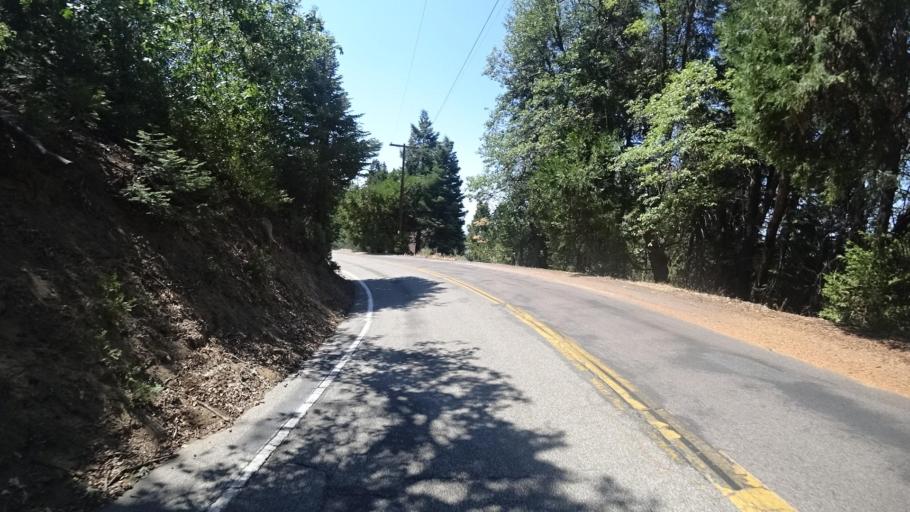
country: US
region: California
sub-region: Riverside County
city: Aguanga
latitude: 33.3140
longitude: -116.8611
